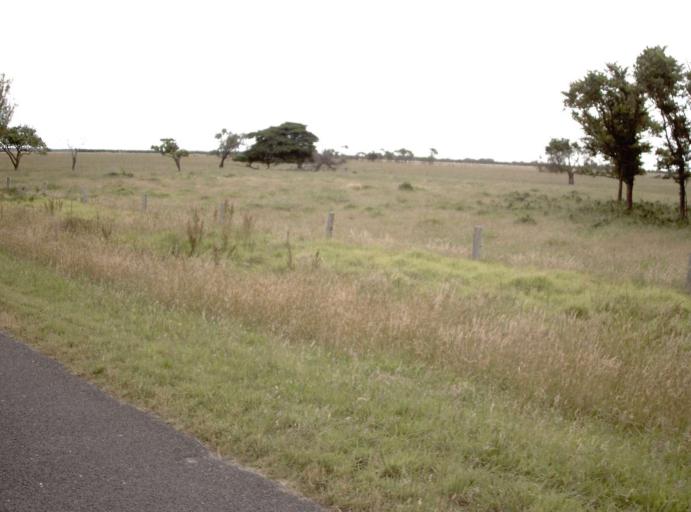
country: AU
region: Victoria
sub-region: Wellington
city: Sale
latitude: -38.5897
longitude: 146.8886
